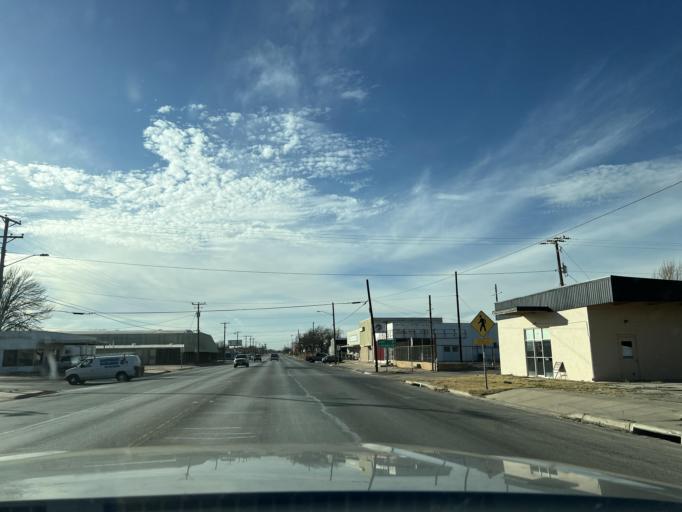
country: US
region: Texas
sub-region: Scurry County
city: Snyder
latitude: 32.7172
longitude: -100.9208
